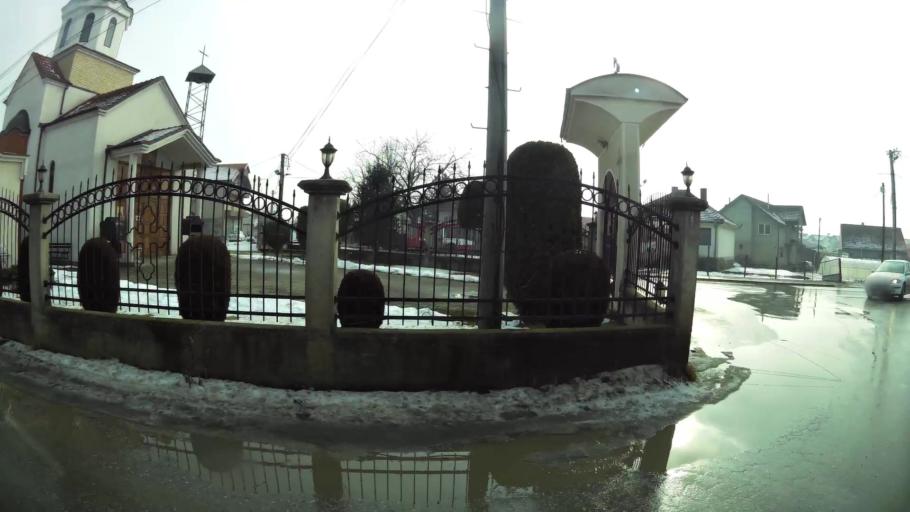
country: MK
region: Ilinden
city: Marino
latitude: 41.9949
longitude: 21.5879
